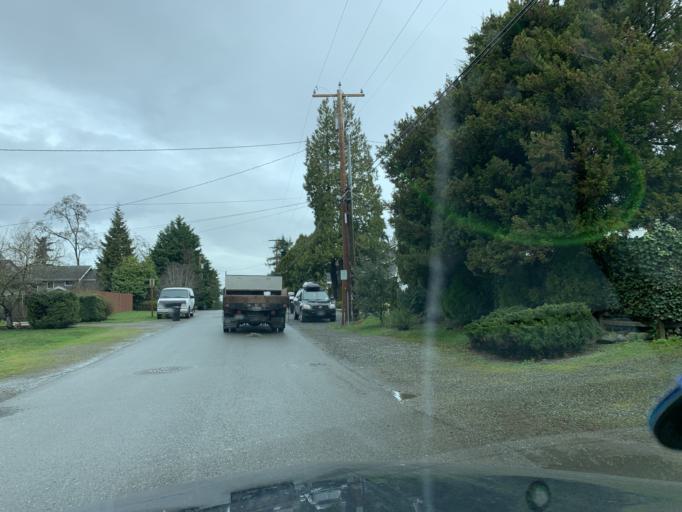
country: US
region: Washington
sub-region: King County
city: Mercer Island
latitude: 47.5900
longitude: -122.2317
